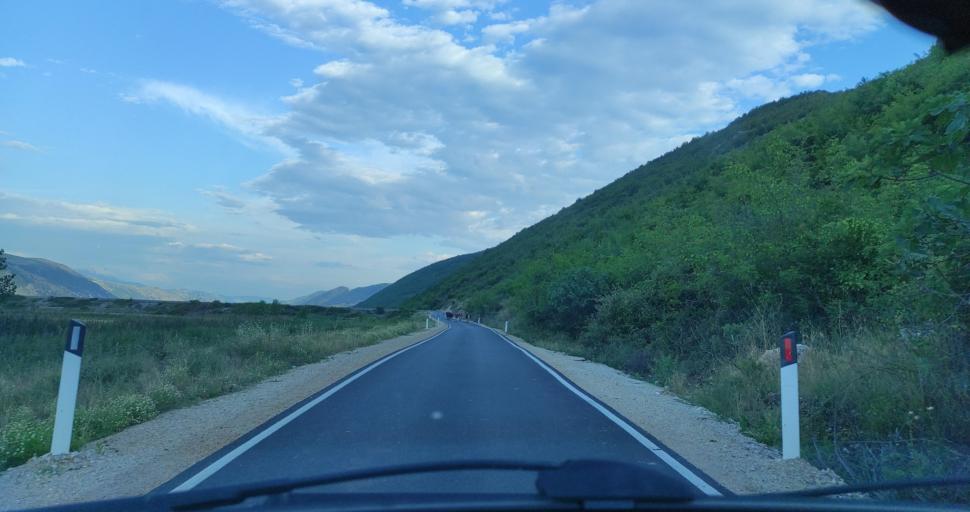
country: AL
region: Shkoder
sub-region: Rrethi i Shkodres
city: Velipoje
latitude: 41.9241
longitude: 19.4509
